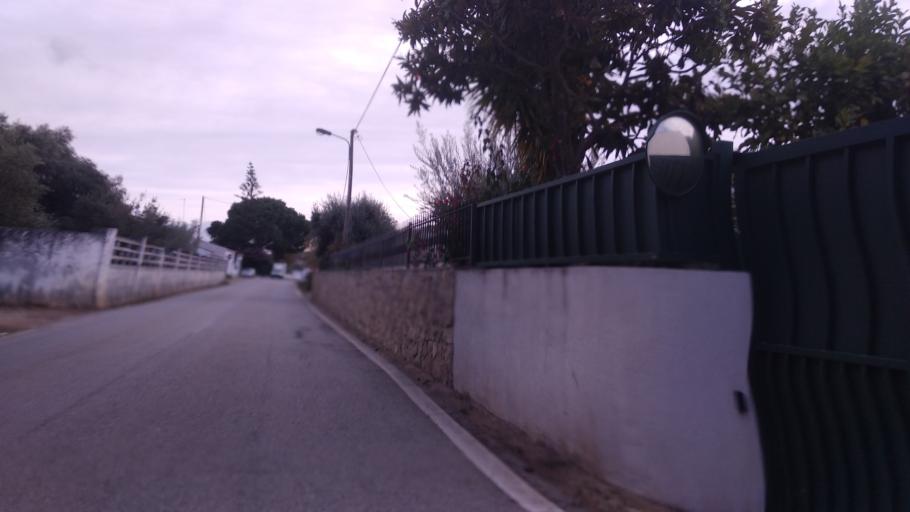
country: PT
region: Faro
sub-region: Sao Bras de Alportel
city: Sao Bras de Alportel
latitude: 37.1732
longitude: -7.9089
